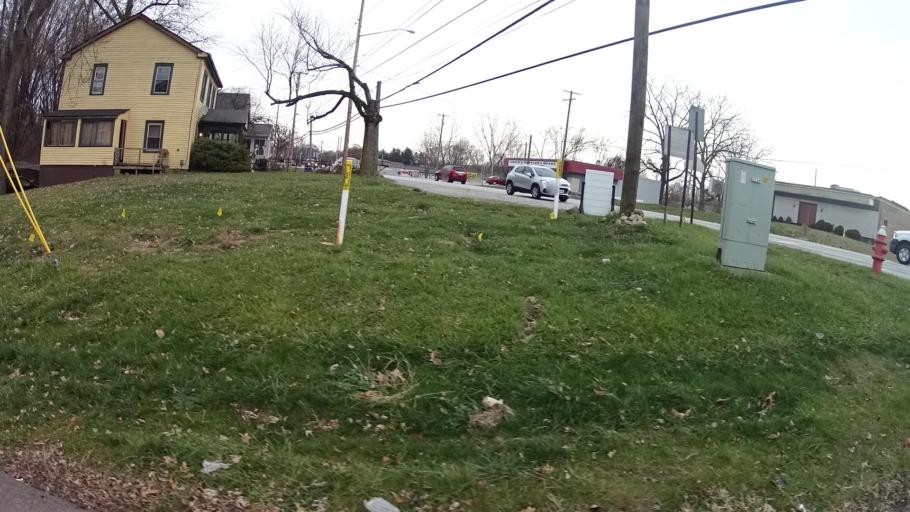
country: US
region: Ohio
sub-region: Lorain County
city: North Ridgeville
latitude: 41.3923
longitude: -82.0111
